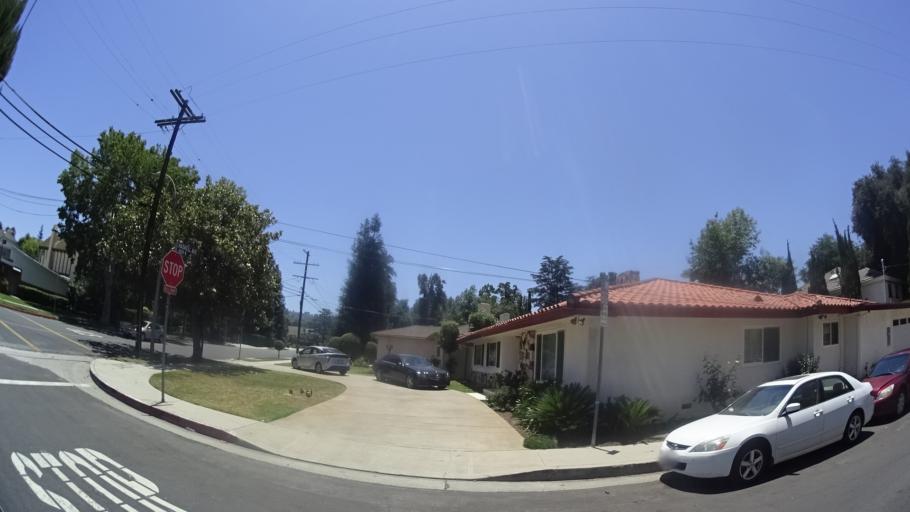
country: US
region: California
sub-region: Los Angeles County
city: Sherman Oaks
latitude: 34.1536
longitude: -118.4744
